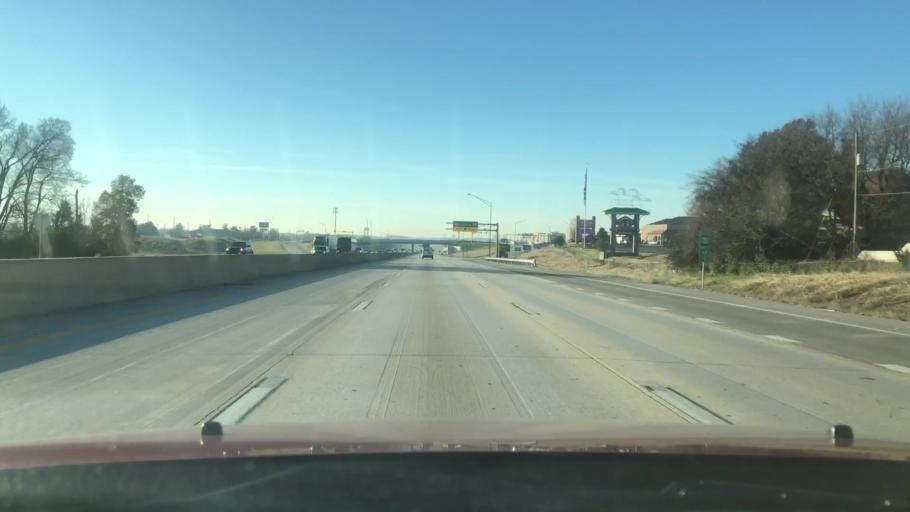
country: US
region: Missouri
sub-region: Greene County
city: Springfield
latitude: 37.1624
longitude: -93.2246
